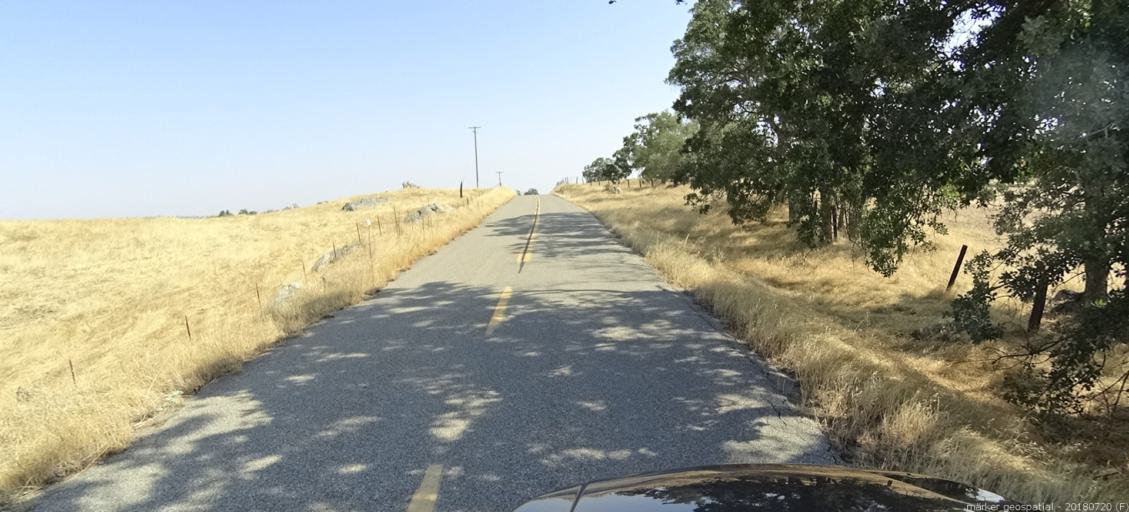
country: US
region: California
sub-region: Madera County
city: Yosemite Lakes
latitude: 37.2545
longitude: -119.9250
